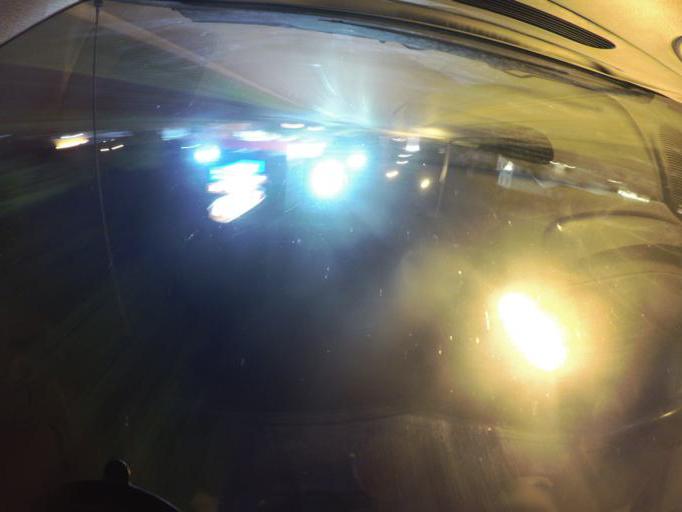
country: US
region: Ohio
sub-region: Ashtabula County
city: Conneaut
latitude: 41.9371
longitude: -80.5816
